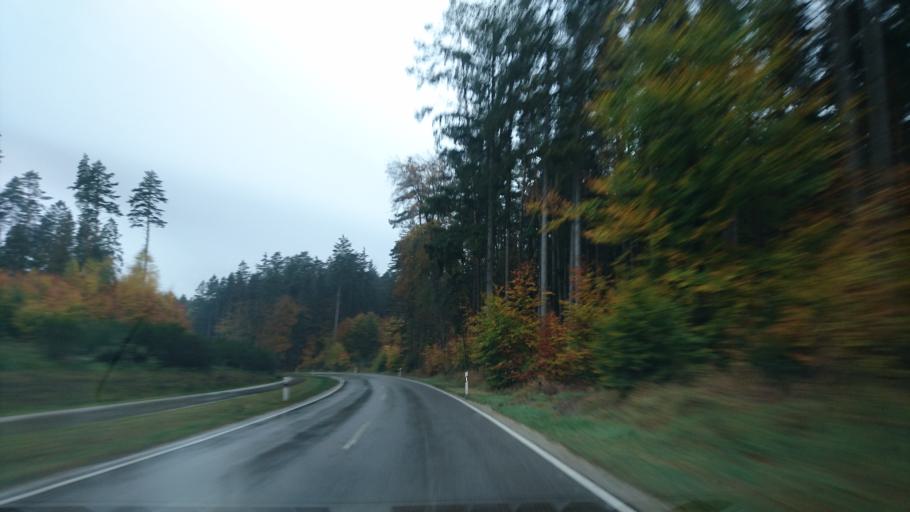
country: DE
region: Bavaria
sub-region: Swabia
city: Kuhbach
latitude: 48.4553
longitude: 11.1808
